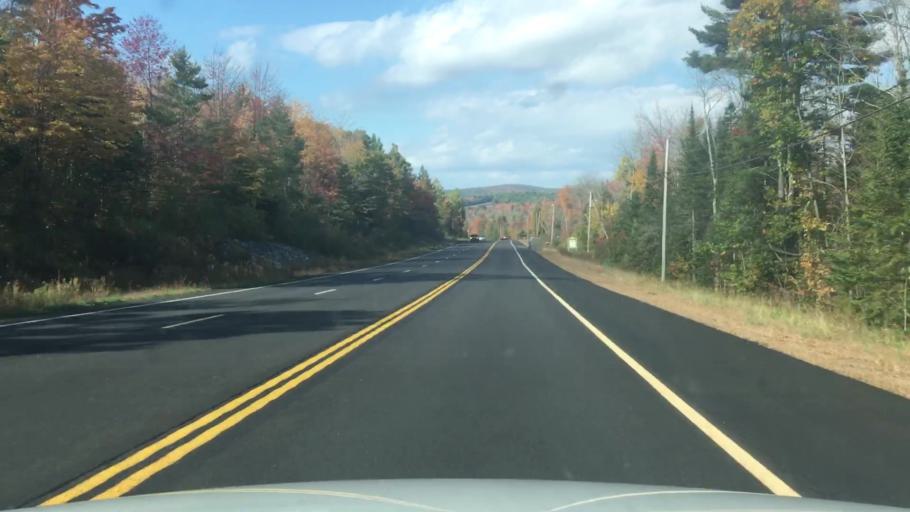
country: US
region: Maine
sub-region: Waldo County
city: Palermo
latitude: 44.3744
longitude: -69.3955
